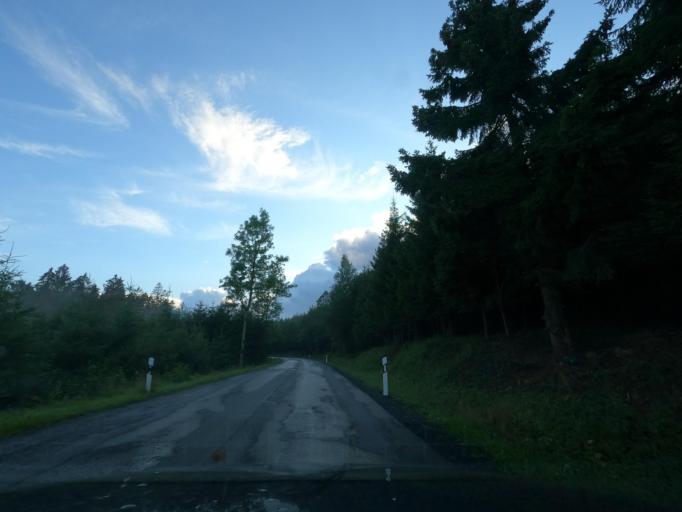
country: DE
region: North Rhine-Westphalia
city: Plettenberg
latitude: 51.2514
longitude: 7.9217
